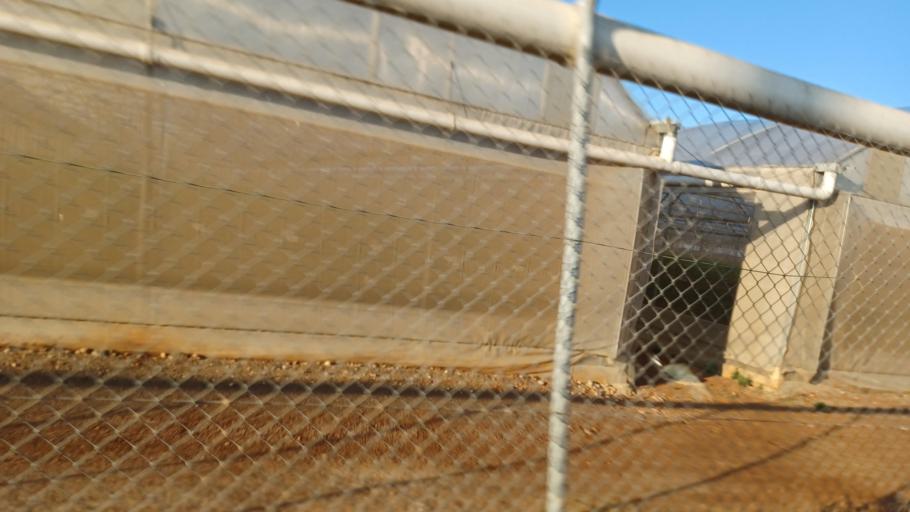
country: CY
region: Ammochostos
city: Avgorou
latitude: 35.0098
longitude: 33.8018
